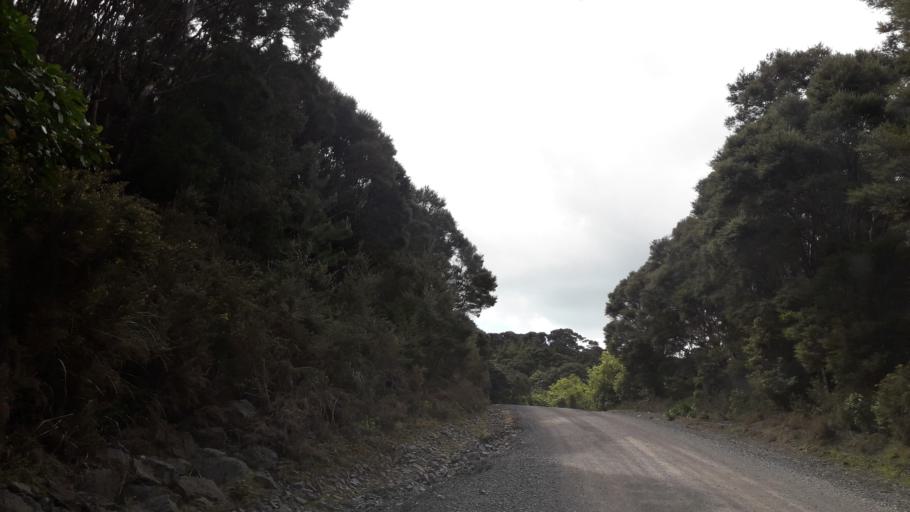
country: NZ
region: Northland
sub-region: Far North District
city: Paihia
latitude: -35.3050
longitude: 174.2207
